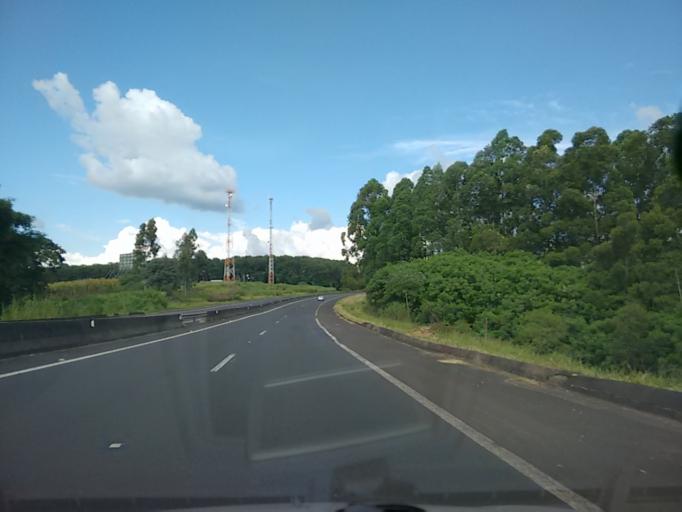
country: BR
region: Sao Paulo
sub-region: Marilia
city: Marilia
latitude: -22.2155
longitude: -49.8480
